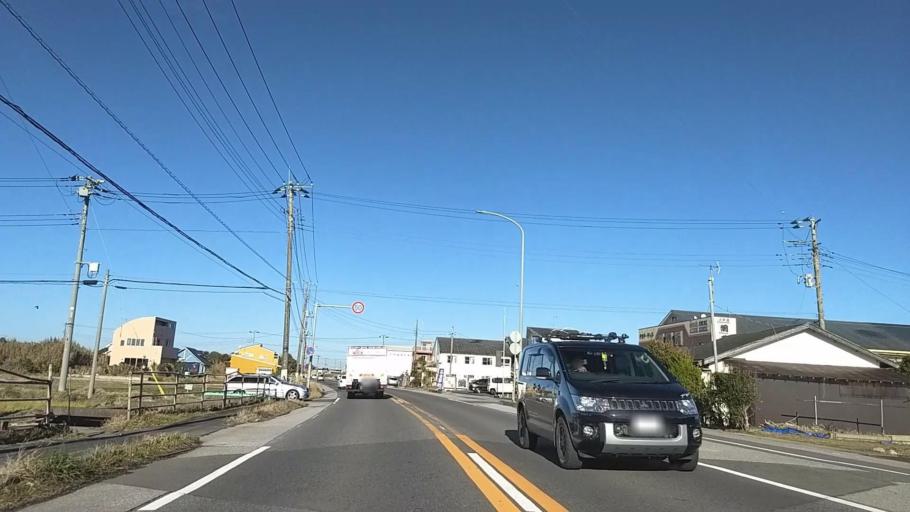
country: JP
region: Chiba
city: Togane
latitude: 35.5182
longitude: 140.4413
